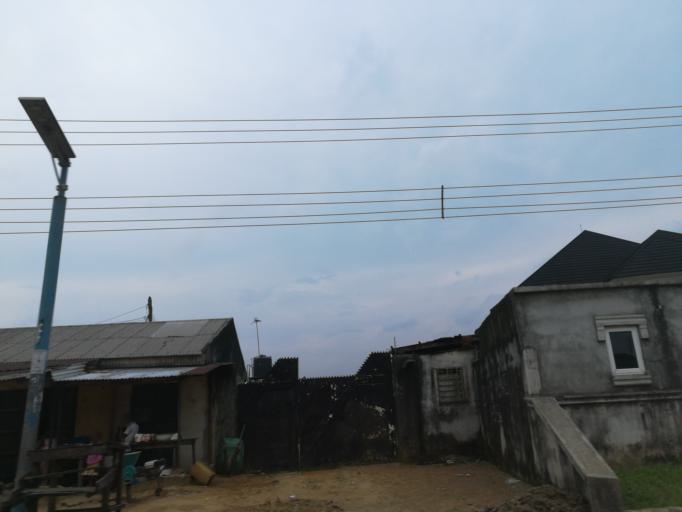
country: NG
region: Rivers
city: Okrika
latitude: 4.7851
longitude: 7.1267
